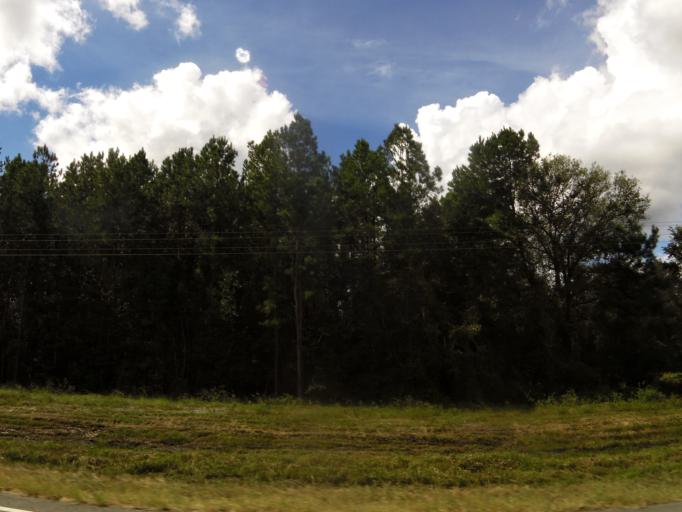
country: US
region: Georgia
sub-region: Brantley County
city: Nahunta
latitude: 31.1135
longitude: -82.0037
